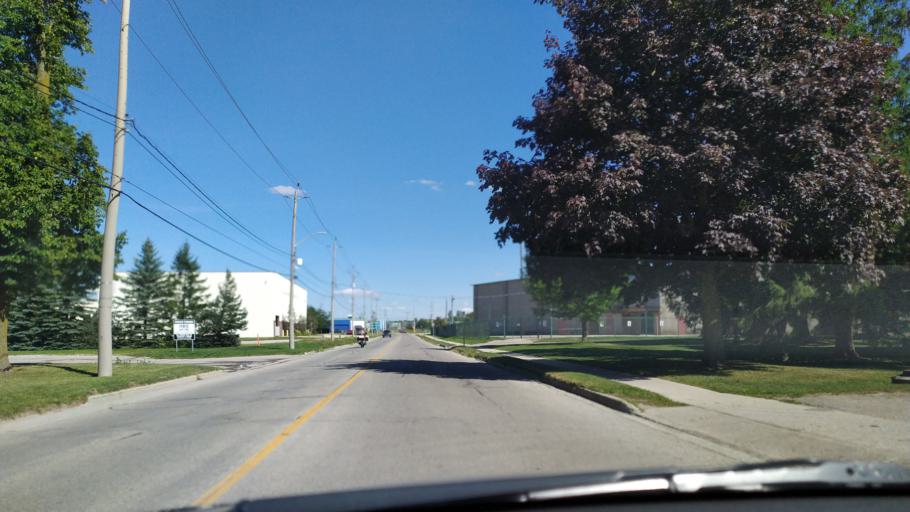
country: CA
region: Ontario
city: Stratford
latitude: 43.3602
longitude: -80.9664
